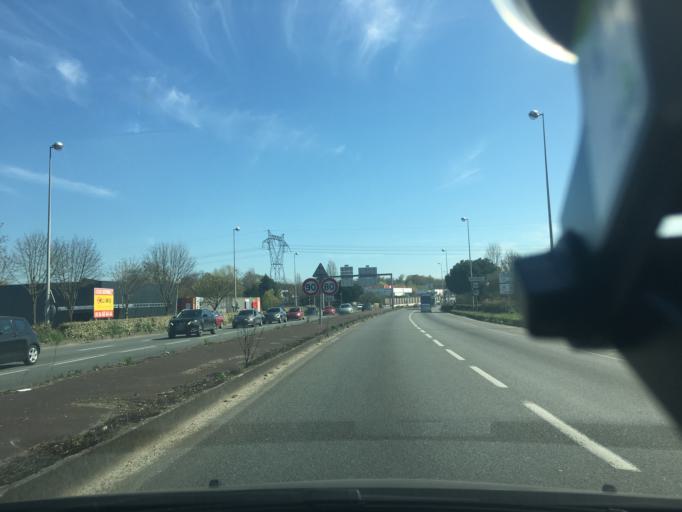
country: FR
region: Aquitaine
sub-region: Departement de la Gironde
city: Lormont
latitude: 44.8687
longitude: -0.5021
